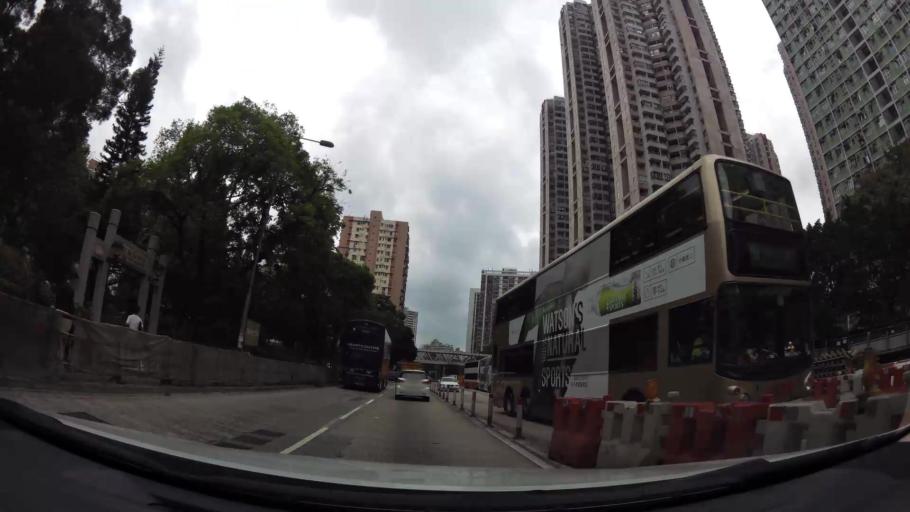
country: HK
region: Wong Tai Sin
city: Wong Tai Sin
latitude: 22.3380
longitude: 114.1959
